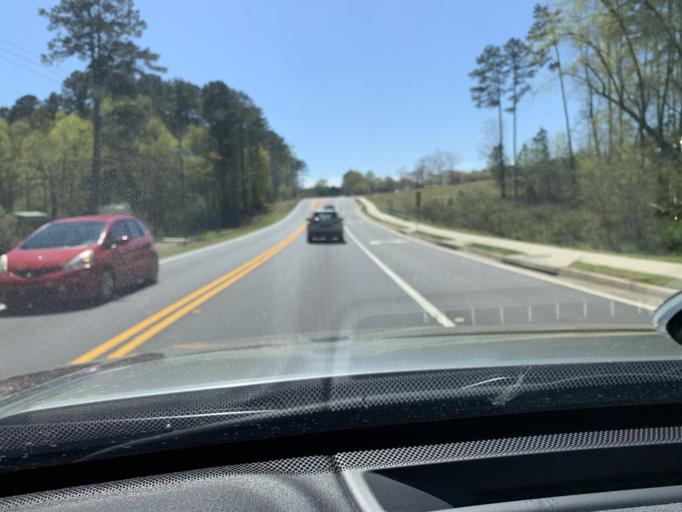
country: US
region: Georgia
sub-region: Forsyth County
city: Cumming
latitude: 34.1793
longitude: -84.2206
